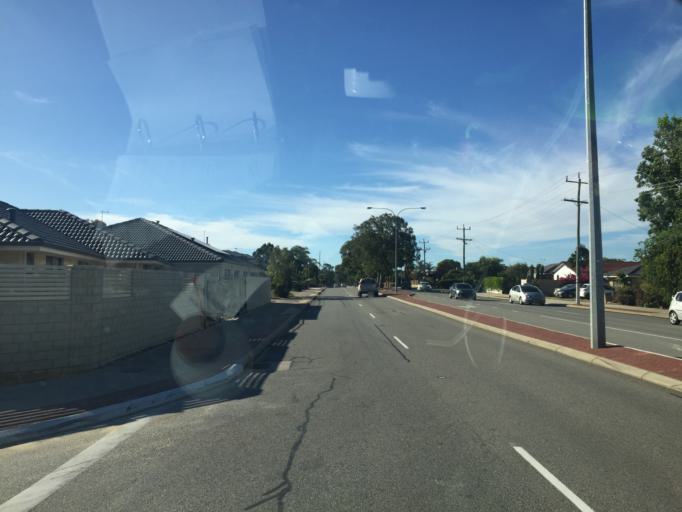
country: AU
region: Western Australia
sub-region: Belmont
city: Kewdale
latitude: -31.9661
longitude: 115.9405
